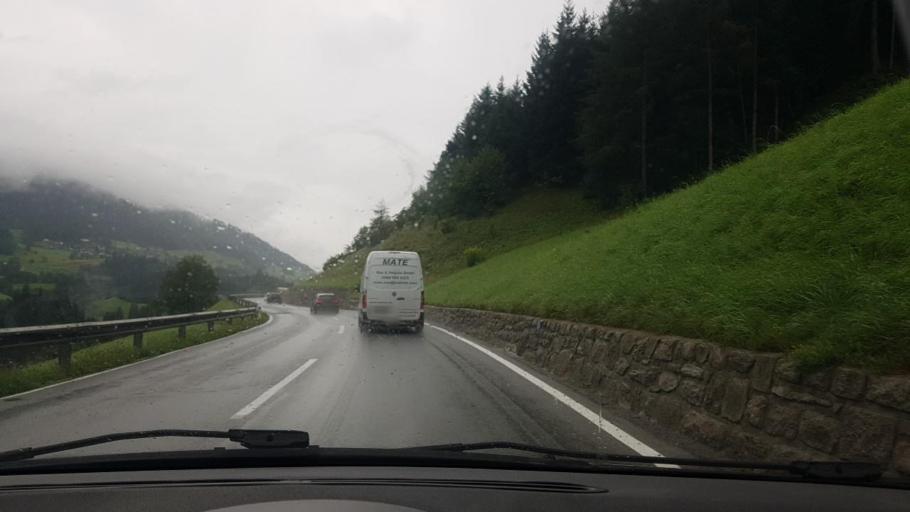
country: AT
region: Tyrol
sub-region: Politischer Bezirk Innsbruck Land
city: Ellbogen
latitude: 47.1512
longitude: 11.4461
